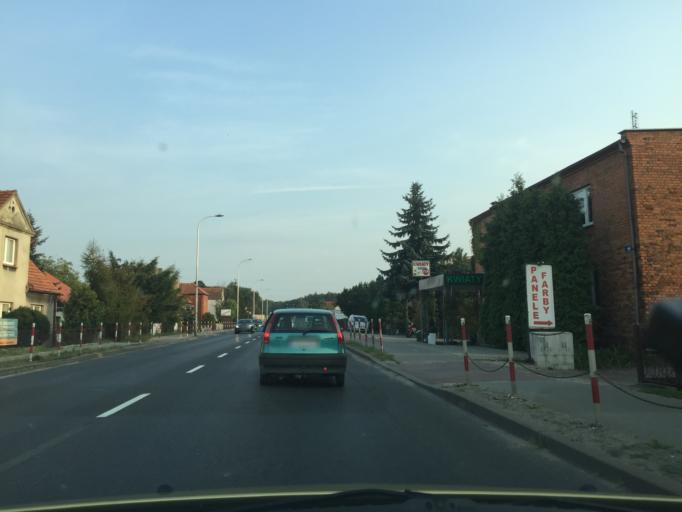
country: PL
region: Greater Poland Voivodeship
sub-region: Powiat jarocinski
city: Jarocin
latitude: 51.9587
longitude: 17.5162
